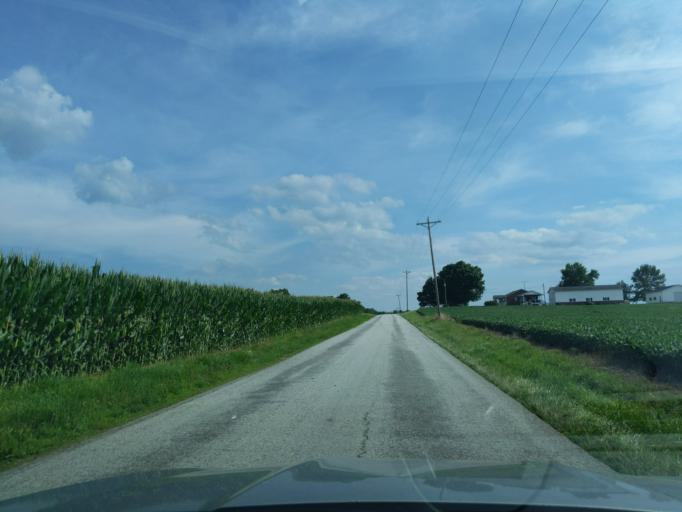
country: US
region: Indiana
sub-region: Decatur County
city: Greensburg
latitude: 39.2550
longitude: -85.4698
